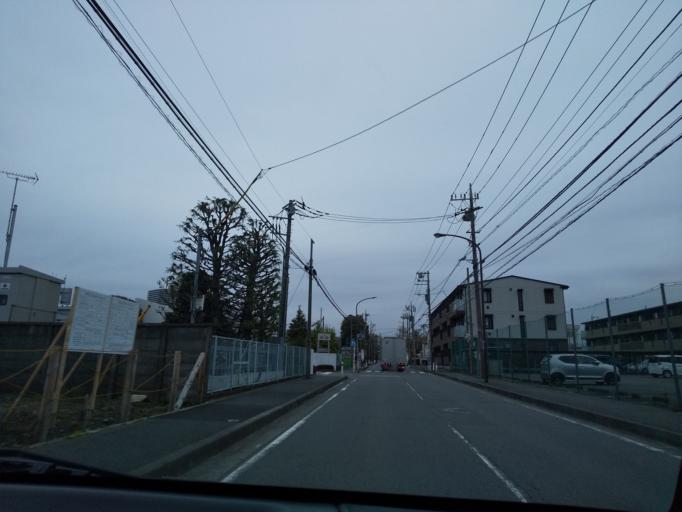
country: JP
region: Tokyo
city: Hachioji
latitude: 35.5905
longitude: 139.3607
